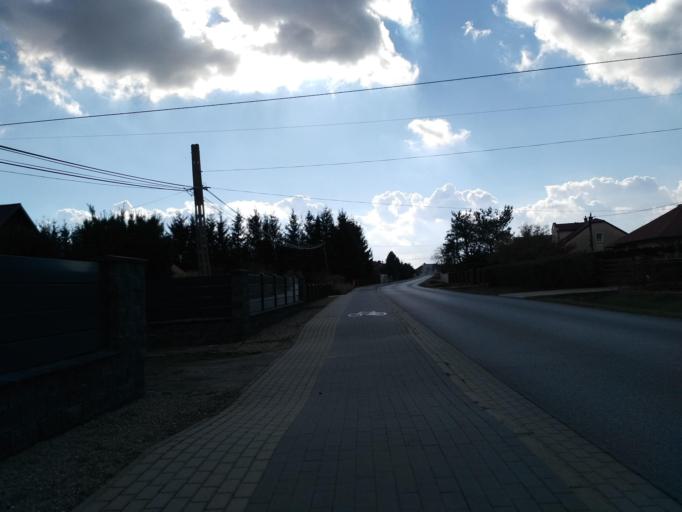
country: PL
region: Subcarpathian Voivodeship
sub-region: Powiat rzeszowski
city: Trzciana
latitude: 50.1122
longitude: 21.8587
